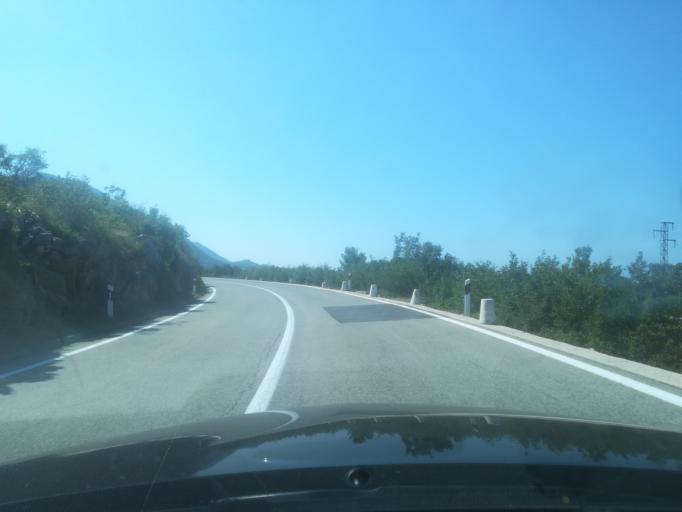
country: HR
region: Primorsko-Goranska
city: Banjol
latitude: 44.7505
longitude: 14.9031
